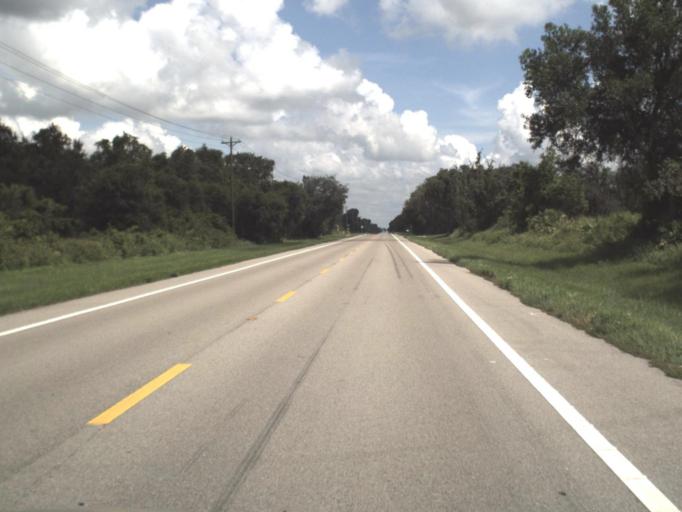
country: US
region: Florida
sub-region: Hillsborough County
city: Wimauma
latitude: 27.4598
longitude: -82.1566
